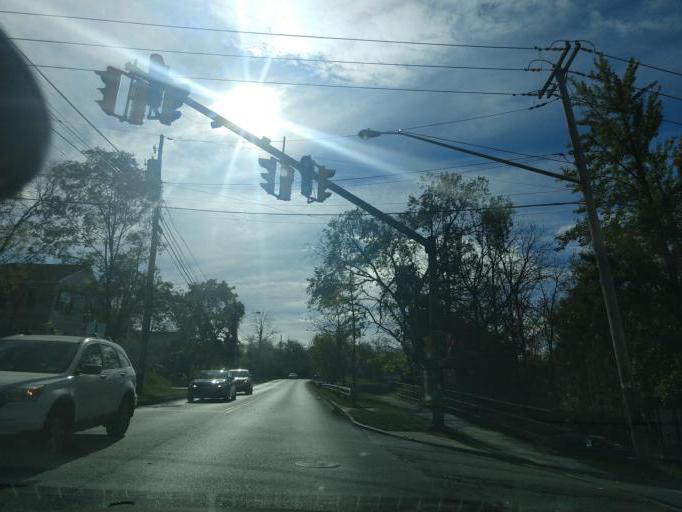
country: US
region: New York
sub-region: Tompkins County
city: South Hill
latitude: 42.4350
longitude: -76.4946
